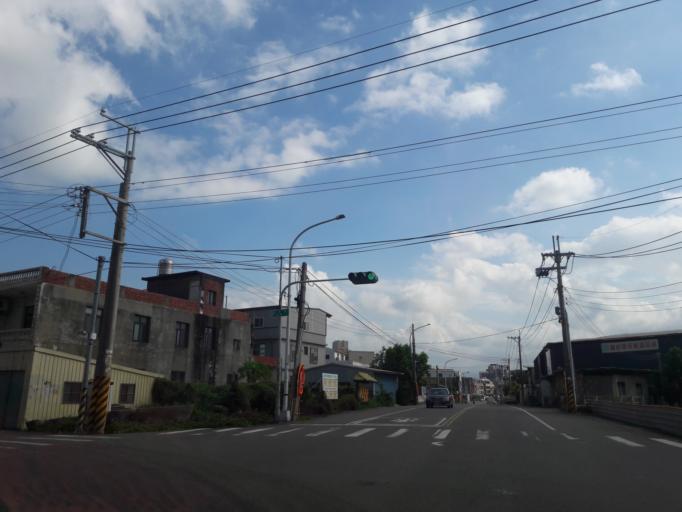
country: TW
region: Taiwan
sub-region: Hsinchu
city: Hsinchu
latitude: 24.7001
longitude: 120.8869
